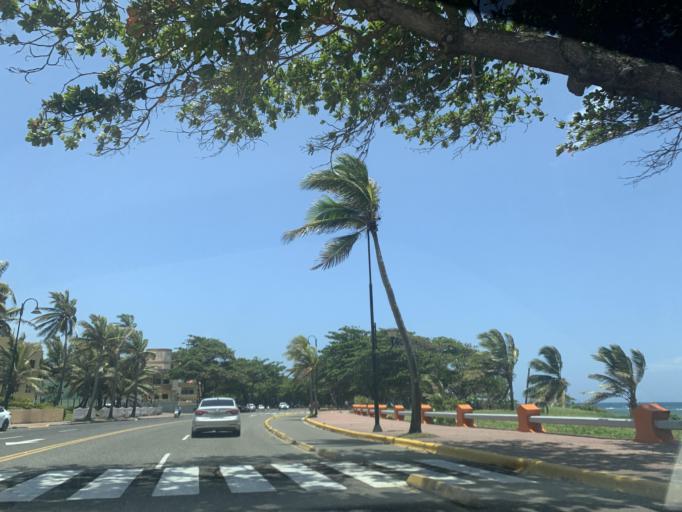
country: DO
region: Puerto Plata
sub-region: Puerto Plata
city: Puerto Plata
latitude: 19.7964
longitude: -70.6847
